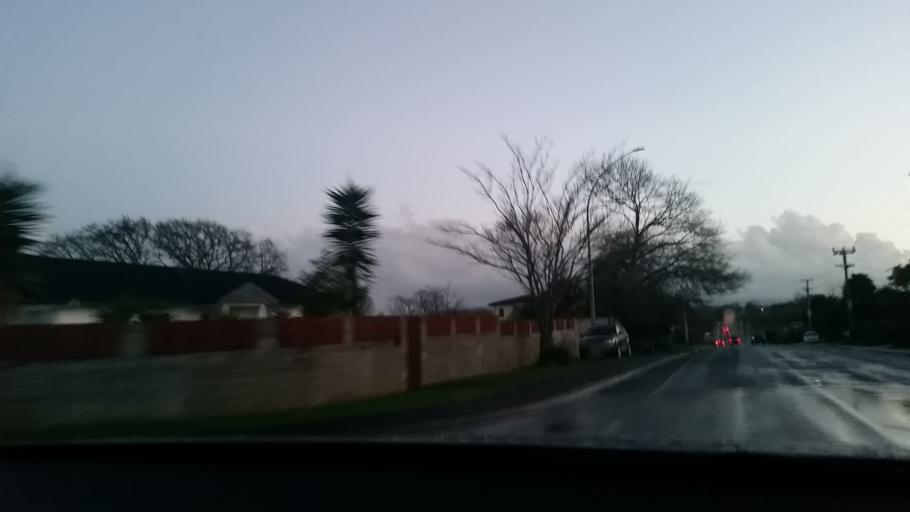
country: NZ
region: Waikato
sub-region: Hamilton City
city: Hamilton
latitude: -37.8037
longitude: 175.2436
